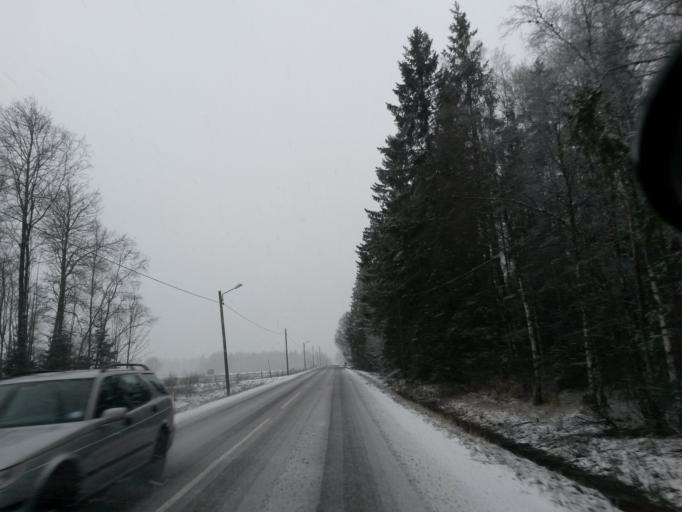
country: SE
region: Vaestra Goetaland
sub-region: Boras Kommun
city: Ganghester
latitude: 57.7579
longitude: 13.0149
